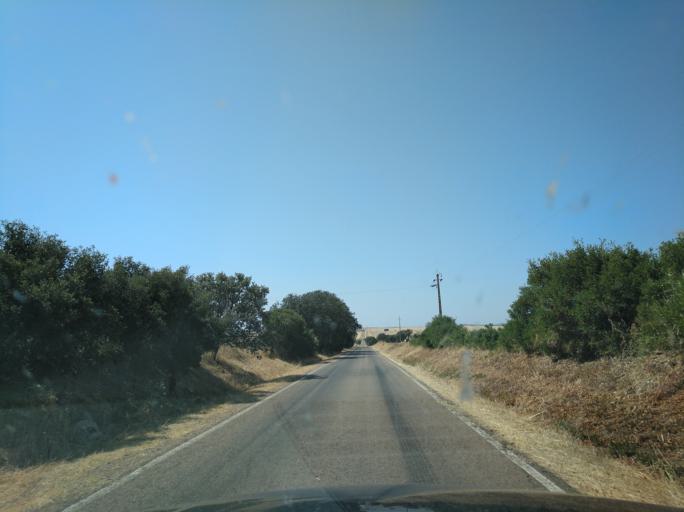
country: PT
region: Portalegre
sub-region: Campo Maior
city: Campo Maior
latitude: 38.9969
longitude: -6.9933
